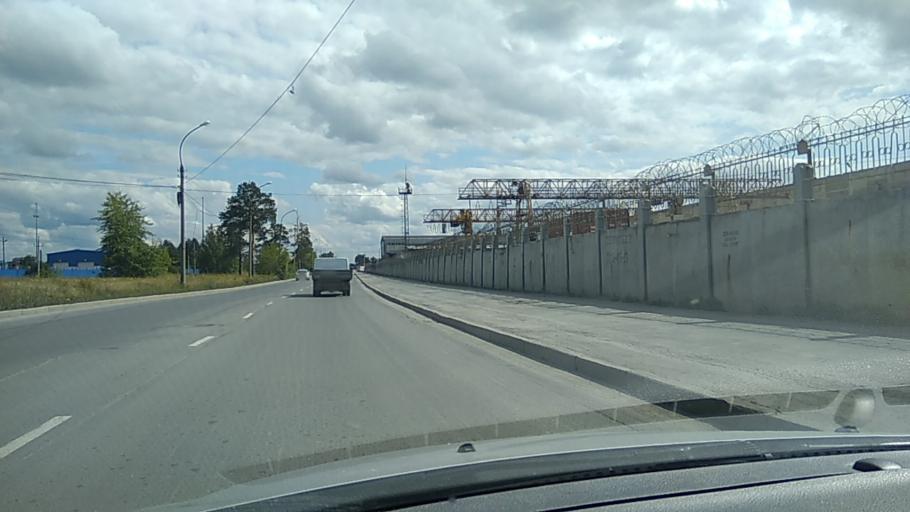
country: RU
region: Sverdlovsk
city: Shuvakish
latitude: 56.8867
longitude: 60.5389
